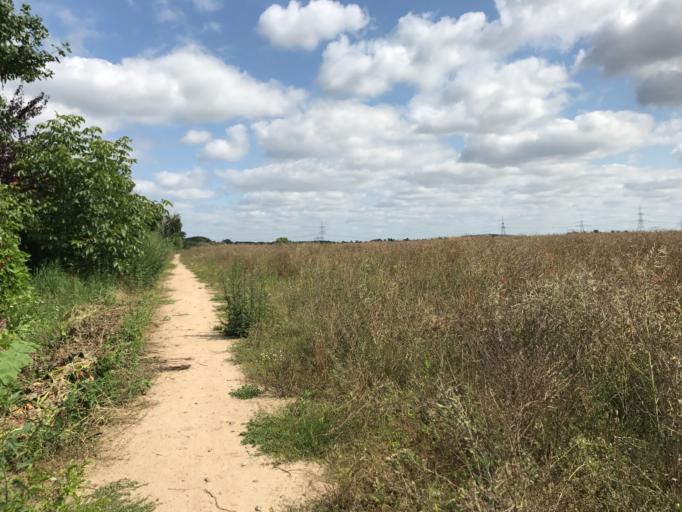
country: DE
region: Berlin
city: Karow
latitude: 52.6136
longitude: 13.5003
